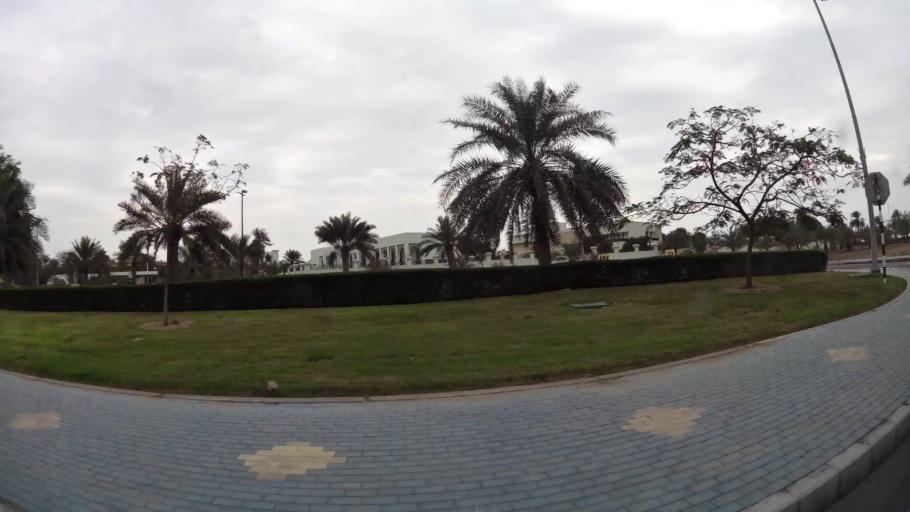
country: AE
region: Abu Dhabi
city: Abu Dhabi
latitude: 24.4315
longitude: 54.3734
